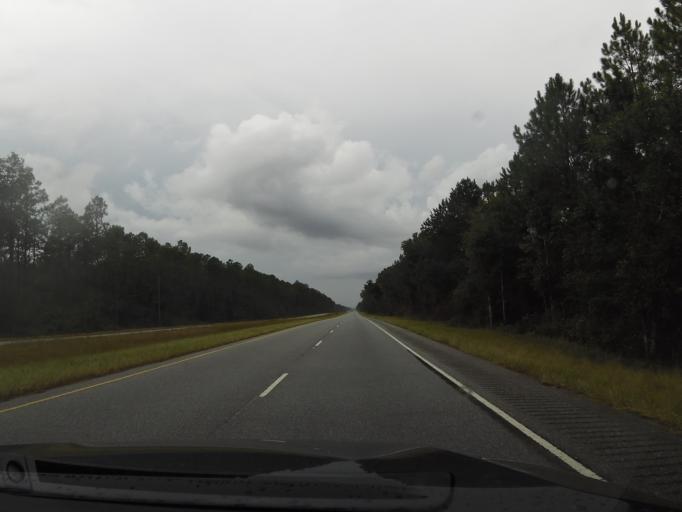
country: US
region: Georgia
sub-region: Wayne County
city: Jesup
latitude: 31.5138
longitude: -81.7703
